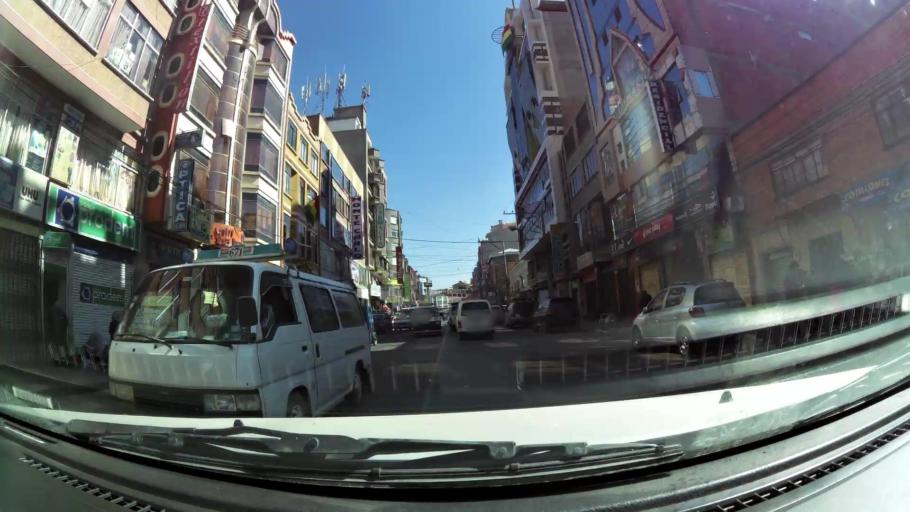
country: BO
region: La Paz
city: La Paz
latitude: -16.5089
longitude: -68.1595
